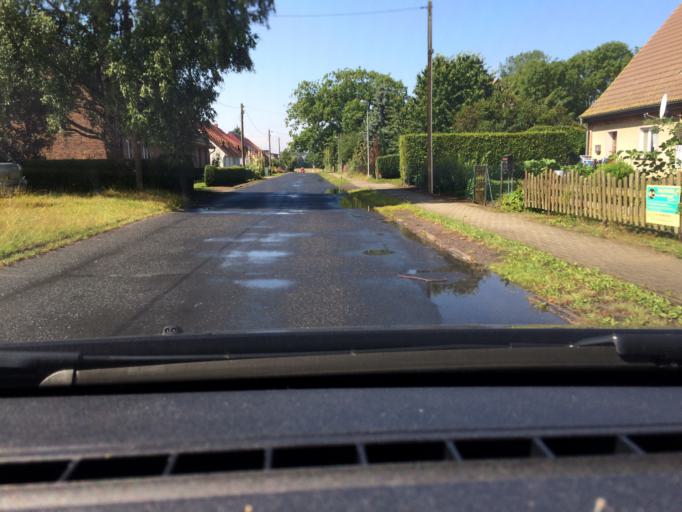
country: DE
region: Mecklenburg-Vorpommern
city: Altenpleen
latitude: 54.3681
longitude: 12.9153
